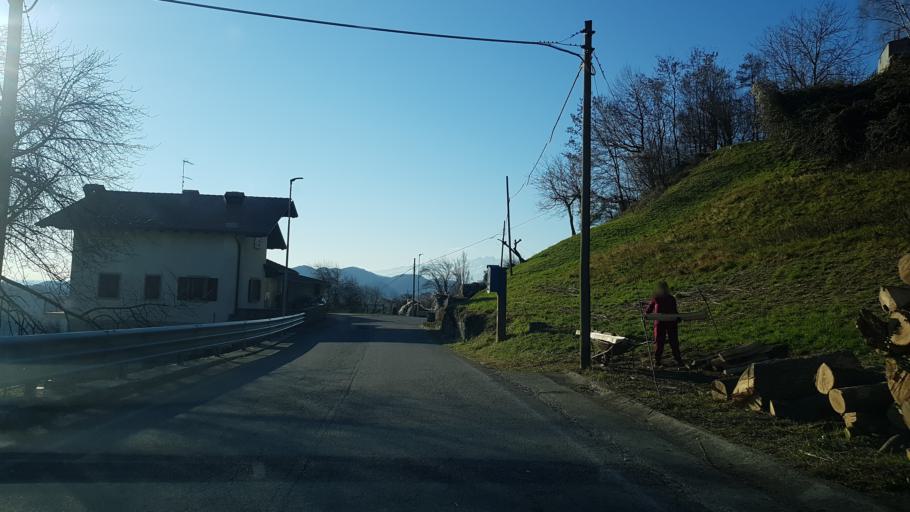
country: IT
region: Friuli Venezia Giulia
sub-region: Provincia di Udine
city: Forgaria nel Friuli
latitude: 46.2257
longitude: 12.9823
